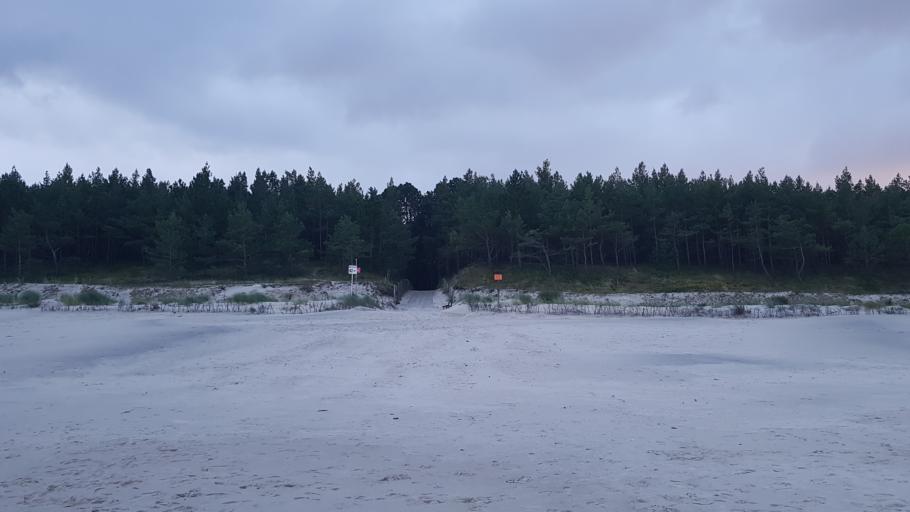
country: PL
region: Pomeranian Voivodeship
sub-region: Powiat pucki
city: Krokowa
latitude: 54.8328
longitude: 18.2154
